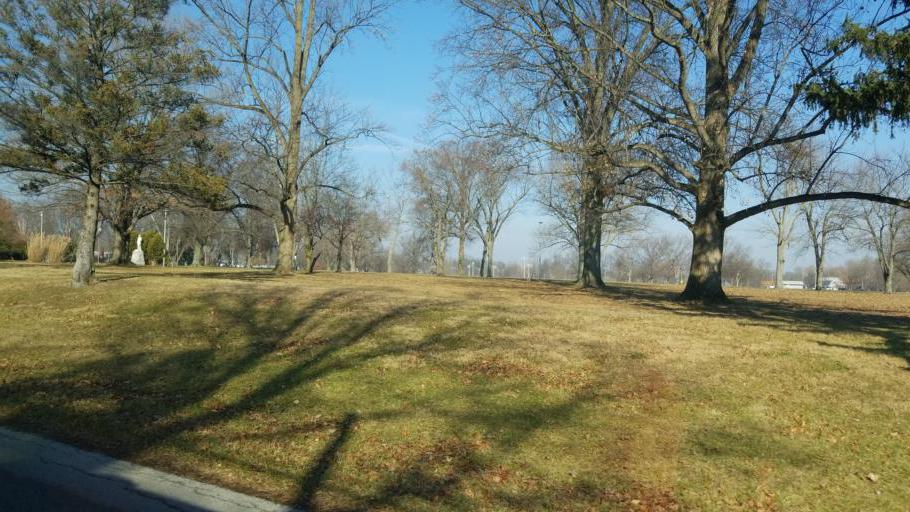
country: US
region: Ohio
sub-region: Seneca County
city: Tiffin
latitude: 41.1021
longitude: -83.1590
